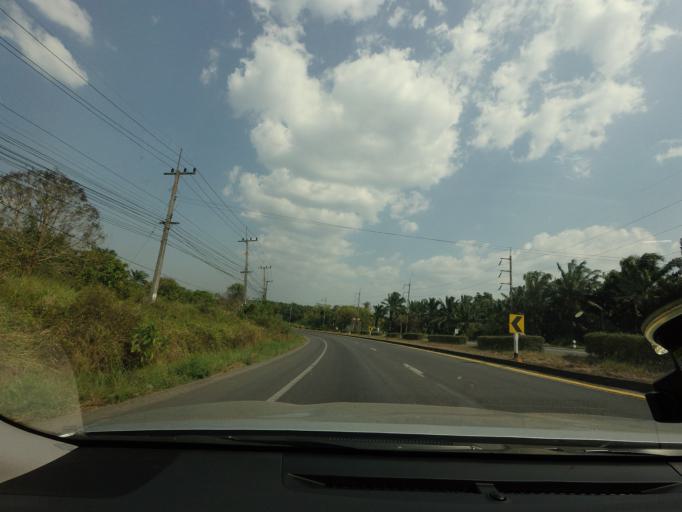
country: TH
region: Phangnga
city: Thap Put
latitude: 8.5096
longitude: 98.6476
